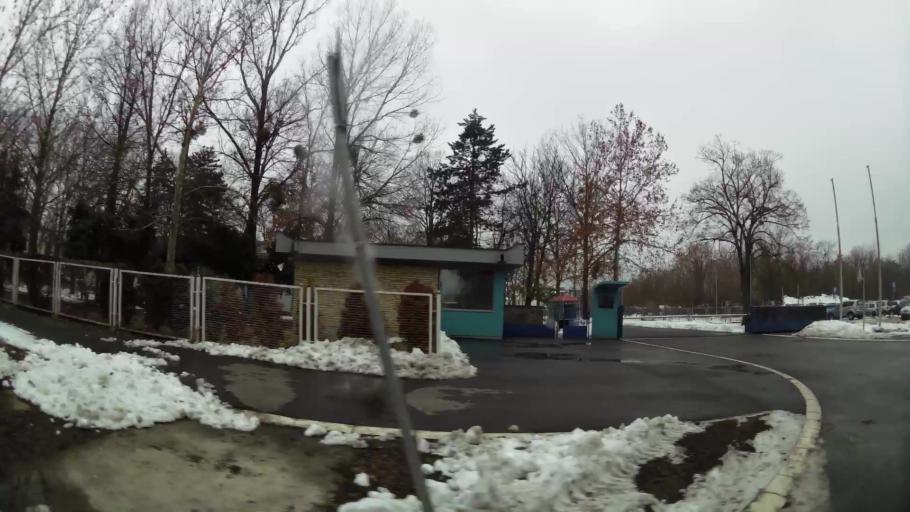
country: RS
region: Central Serbia
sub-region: Belgrade
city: Savski Venac
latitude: 44.7652
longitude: 20.4640
